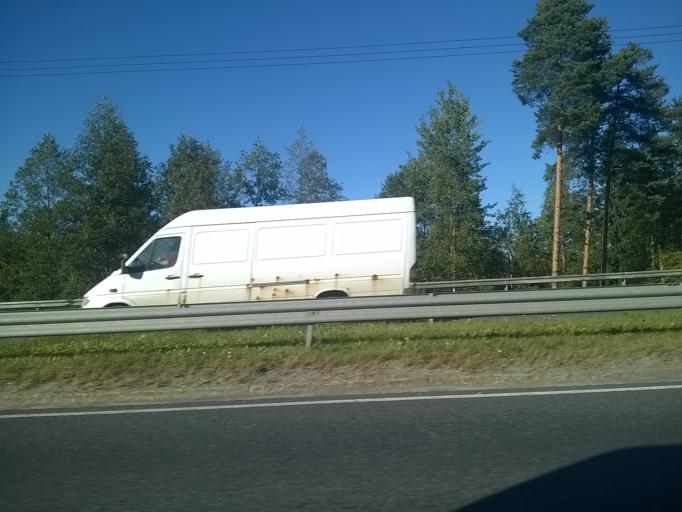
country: FI
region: Pirkanmaa
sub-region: Tampere
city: Tampere
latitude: 61.5025
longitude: 23.8654
